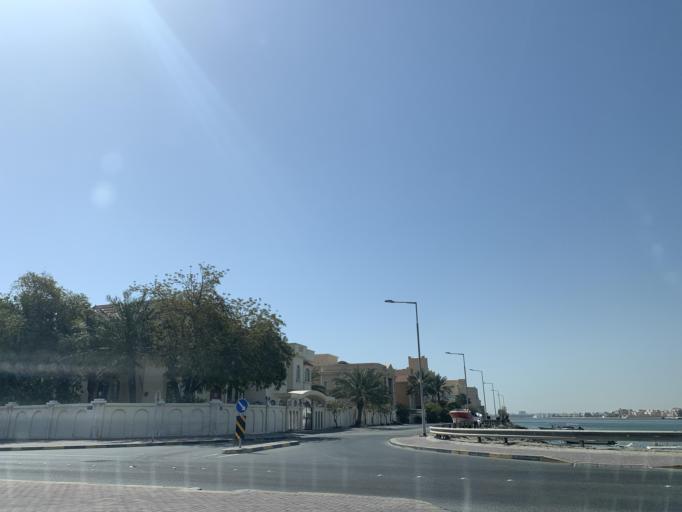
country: BH
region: Manama
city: Manama
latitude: 26.2031
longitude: 50.5682
